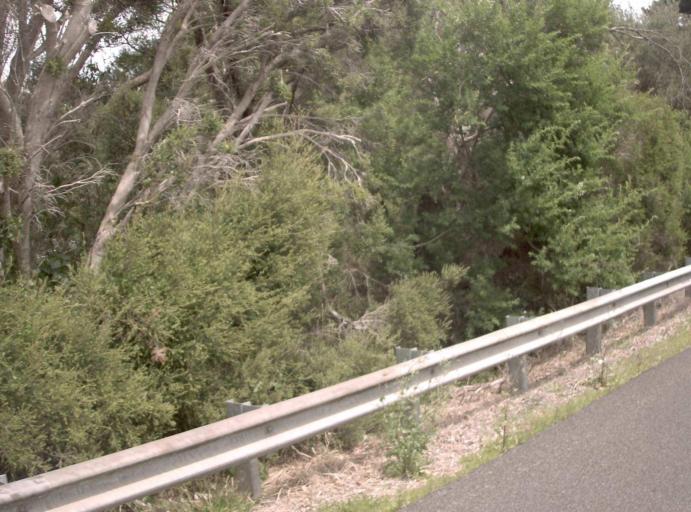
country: AU
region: Victoria
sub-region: Mornington Peninsula
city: Rosebud
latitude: -38.3694
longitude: 144.9107
